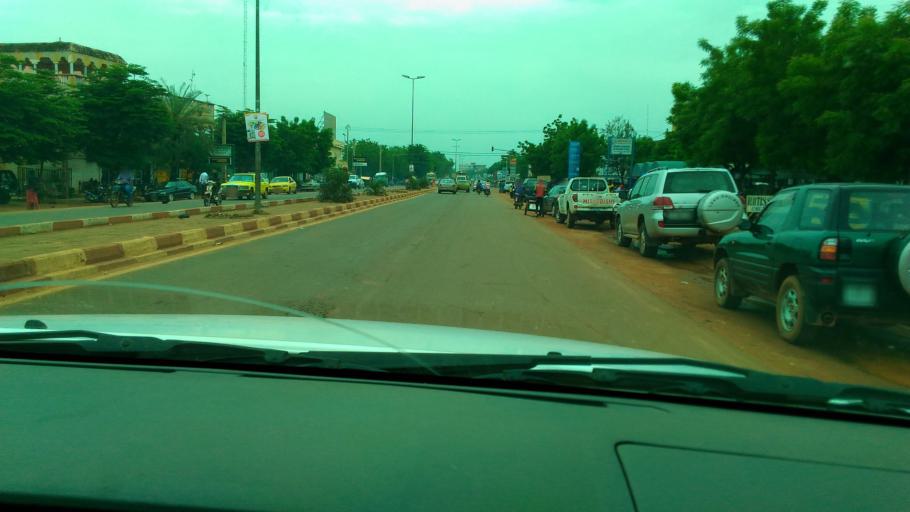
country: ML
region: Bamako
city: Bamako
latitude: 12.5733
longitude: -7.9838
